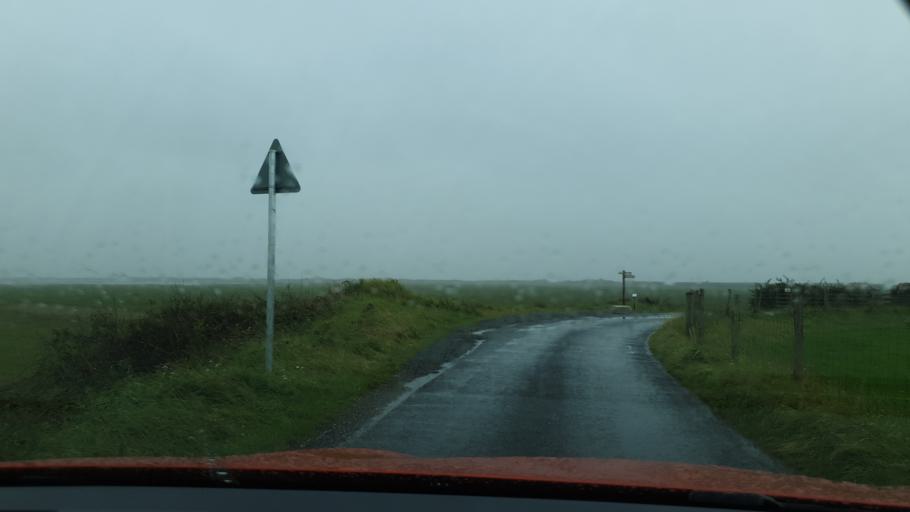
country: GB
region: England
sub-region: Cumbria
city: Barrow in Furness
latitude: 54.0592
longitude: -3.2079
